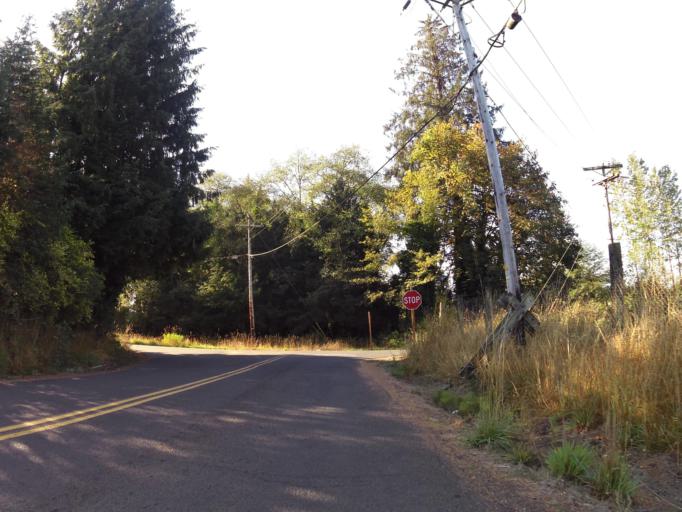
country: US
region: Oregon
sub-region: Tillamook County
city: Tillamook
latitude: 45.4017
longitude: -123.7934
